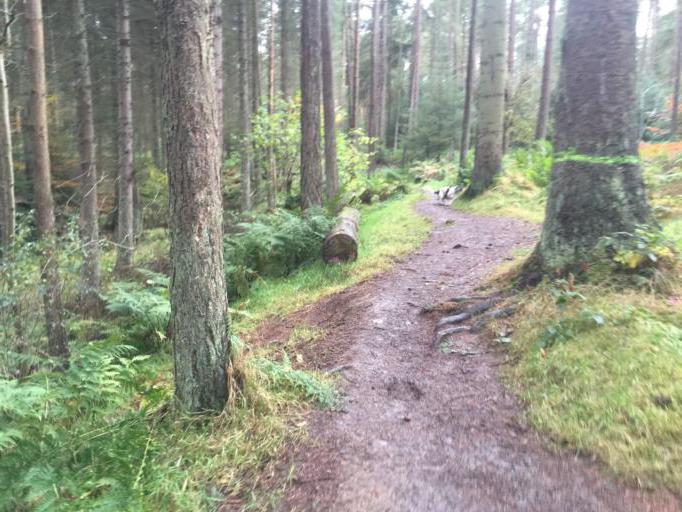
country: GB
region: Scotland
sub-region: West Lothian
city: Linlithgow
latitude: 55.9485
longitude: -3.5924
